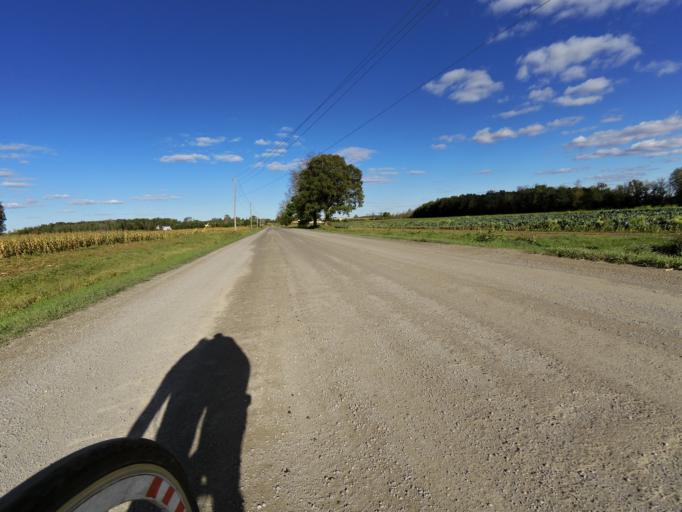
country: CA
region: Ontario
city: Bells Corners
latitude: 45.1237
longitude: -75.6831
